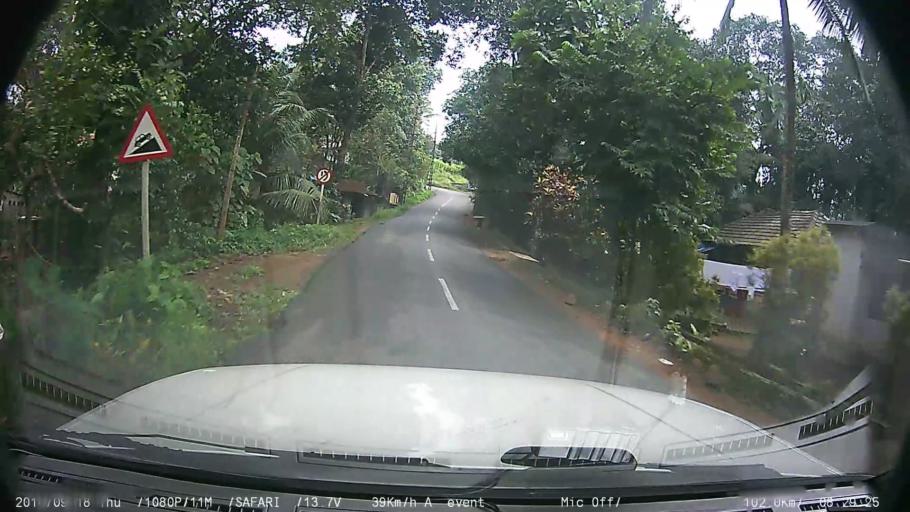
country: IN
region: Kerala
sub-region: Kottayam
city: Palackattumala
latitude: 9.6865
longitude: 76.6108
